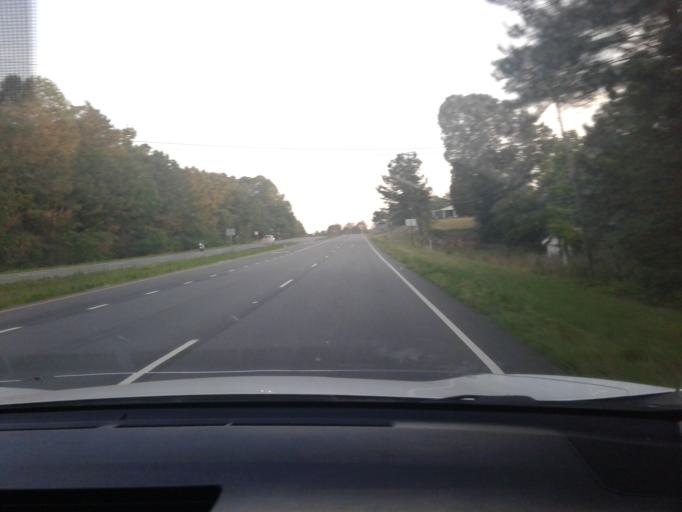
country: US
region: North Carolina
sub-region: Harnett County
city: Buies Creek
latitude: 35.3750
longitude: -78.7102
